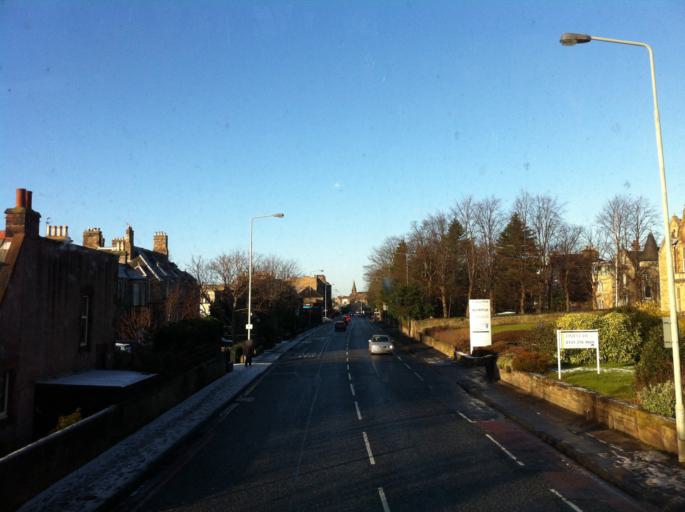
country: GB
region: Scotland
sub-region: Edinburgh
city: Colinton
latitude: 55.9421
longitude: -3.2765
